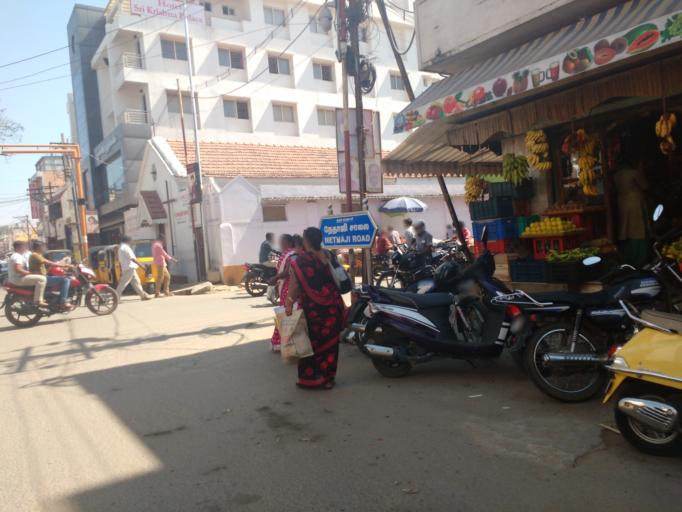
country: IN
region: Tamil Nadu
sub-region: Krishnagiri
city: Hosur
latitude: 12.7322
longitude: 77.8285
